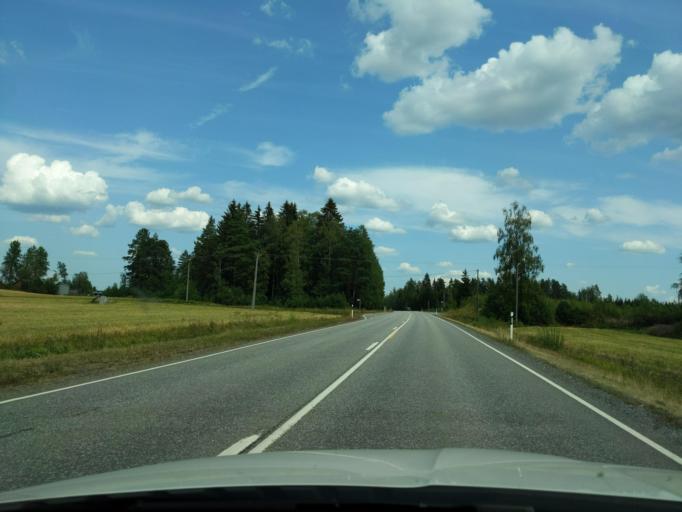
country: FI
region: Haeme
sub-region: Haemeenlinna
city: Lammi
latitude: 61.1180
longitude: 24.9352
